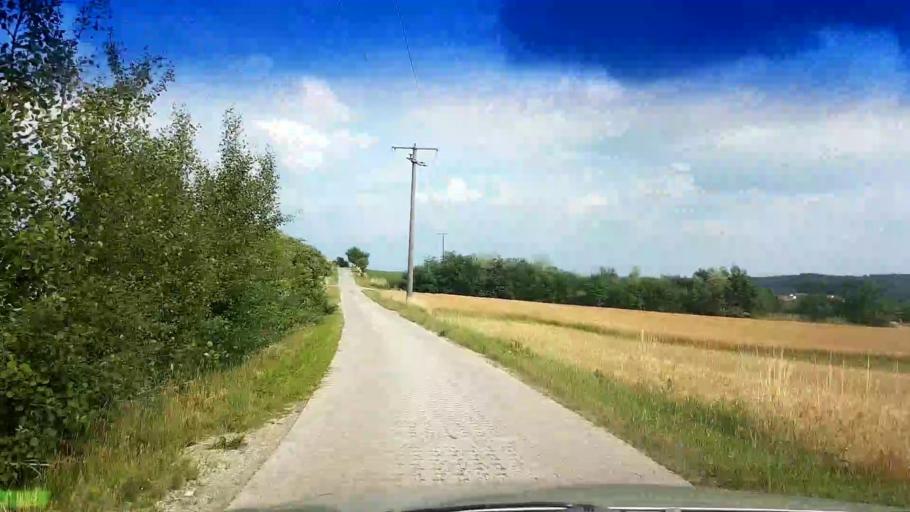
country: DE
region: Bavaria
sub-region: Upper Franconia
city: Walsdorf
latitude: 49.8755
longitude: 10.8035
